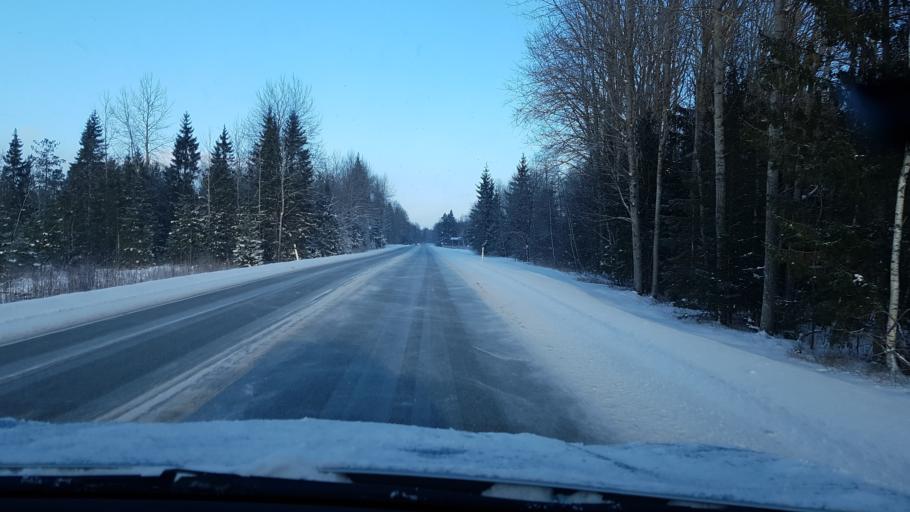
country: EE
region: Harju
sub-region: Nissi vald
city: Riisipere
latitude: 59.1632
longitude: 24.3460
